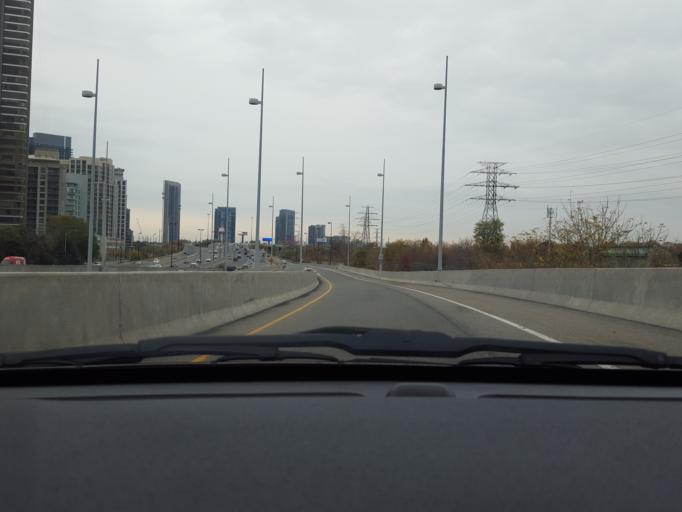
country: CA
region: Ontario
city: Toronto
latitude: 43.6339
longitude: -79.4732
